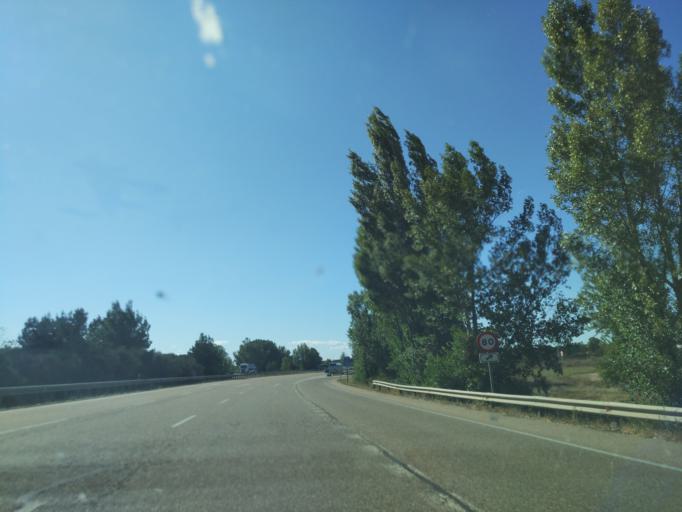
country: ES
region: Castille and Leon
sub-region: Provincia de Zamora
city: Castrogonzalo
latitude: 41.9867
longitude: -5.6324
